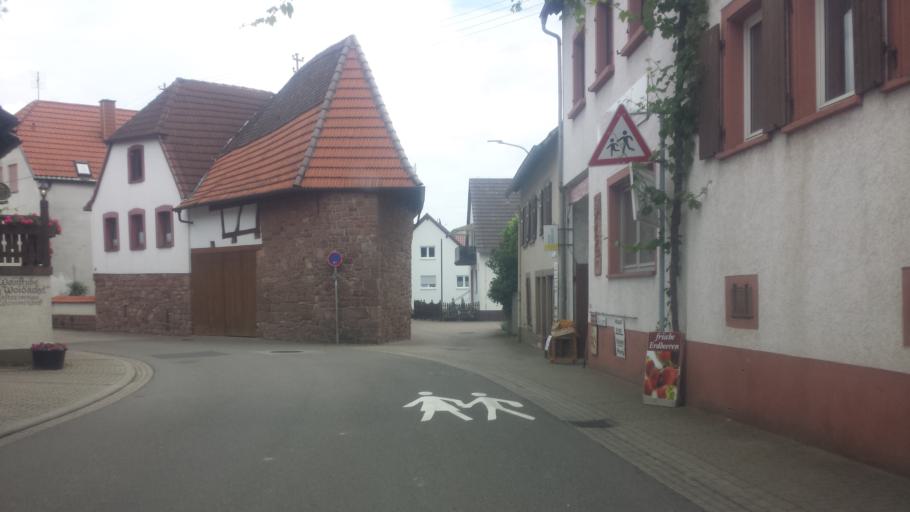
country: DE
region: Rheinland-Pfalz
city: Ranschbach
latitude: 49.1964
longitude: 8.0296
